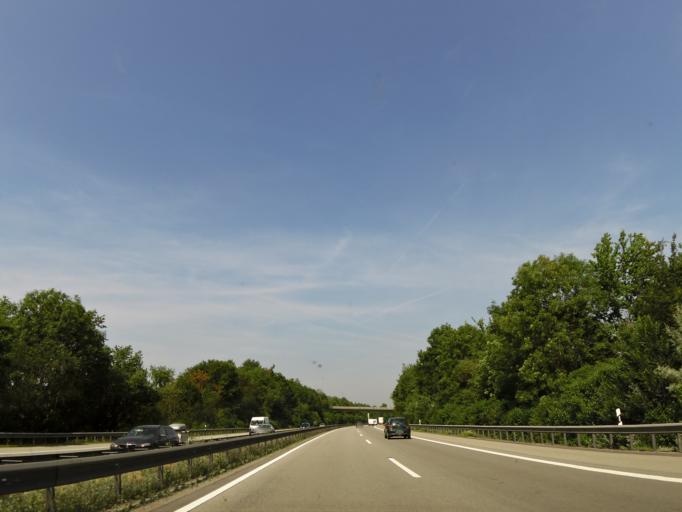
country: DE
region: Rheinland-Pfalz
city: Gau-Bickelheim
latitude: 49.8303
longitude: 8.0235
